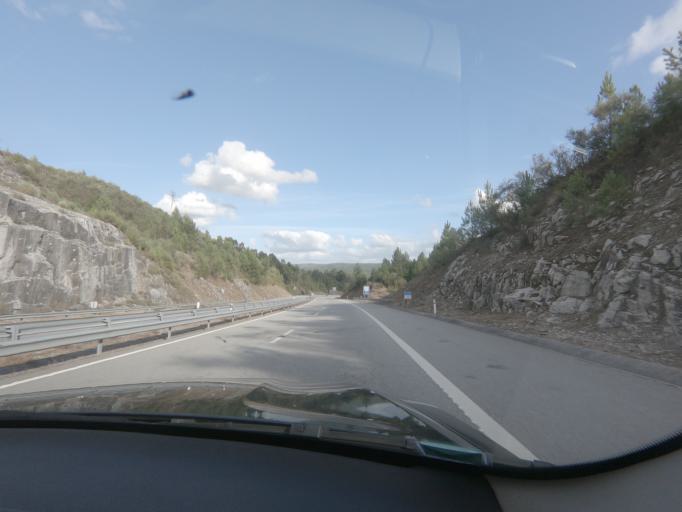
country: PT
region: Viseu
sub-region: Castro Daire
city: Castro Daire
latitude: 40.8079
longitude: -7.9366
